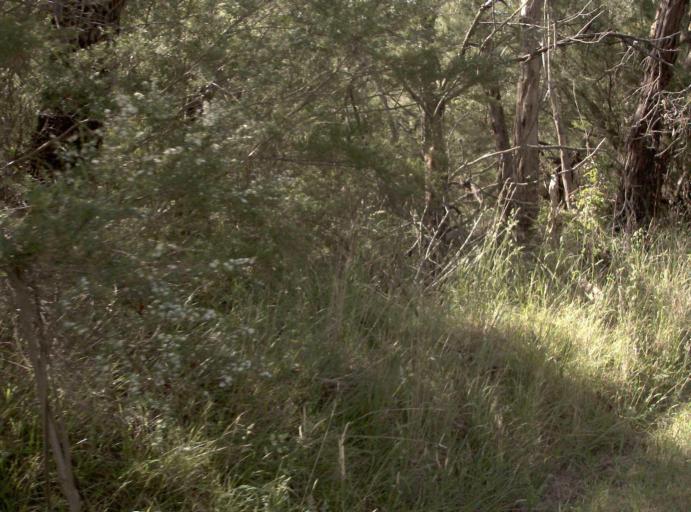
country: AU
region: Victoria
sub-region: Latrobe
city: Morwell
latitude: -38.1907
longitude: 146.4039
